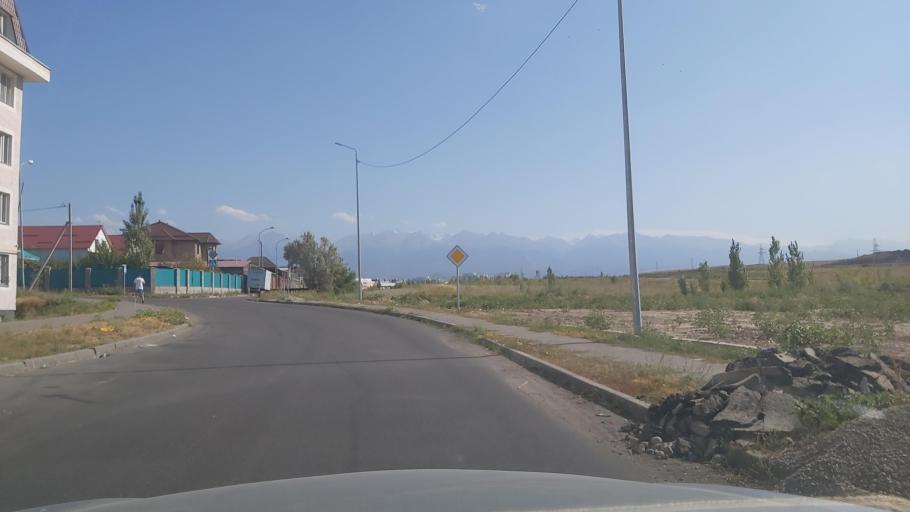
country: KZ
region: Almaty Oblysy
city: Burunday
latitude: 43.3191
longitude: 76.8390
